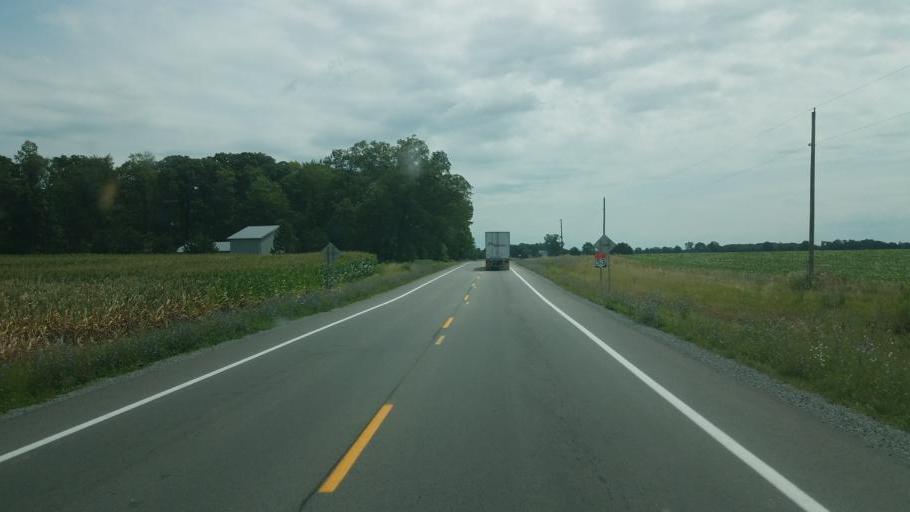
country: US
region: Ohio
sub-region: Wyandot County
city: Upper Sandusky
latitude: 40.8617
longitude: -83.2766
